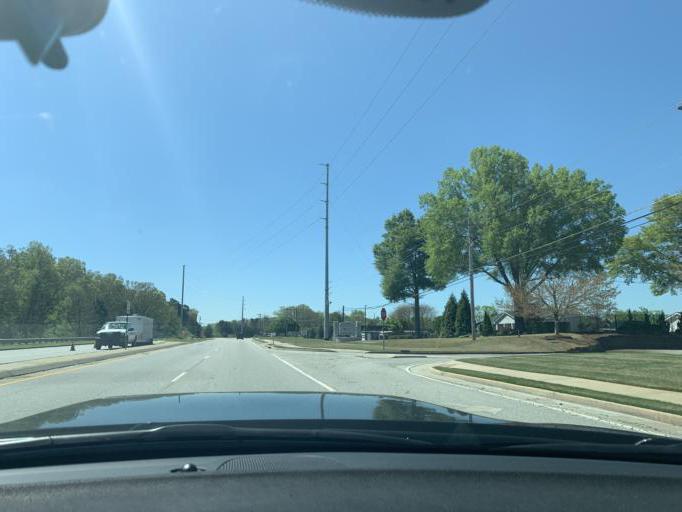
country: US
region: Georgia
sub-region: Forsyth County
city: Cumming
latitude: 34.1601
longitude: -84.1533
